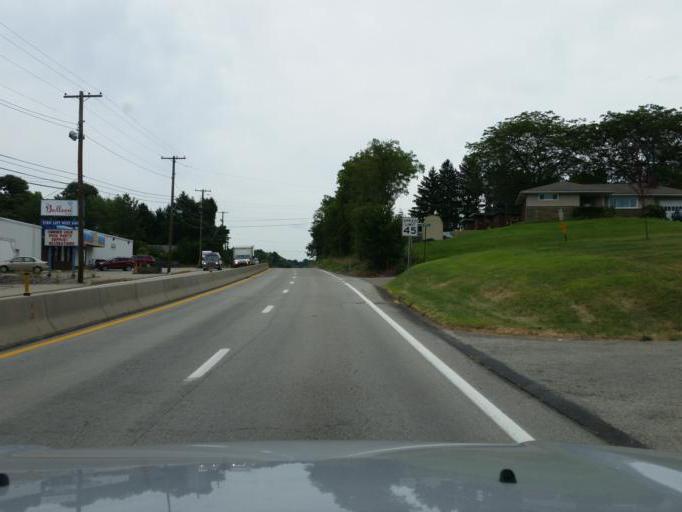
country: US
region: Pennsylvania
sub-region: Westmoreland County
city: Jeannette
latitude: 40.3093
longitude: -79.6346
